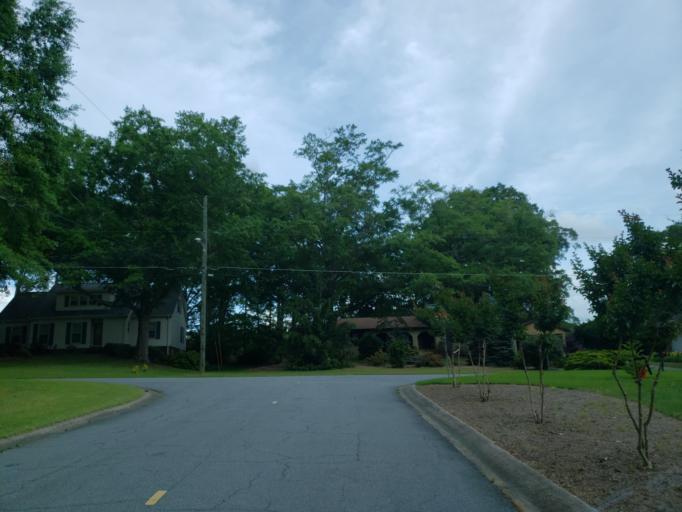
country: US
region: Georgia
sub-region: Cobb County
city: Marietta
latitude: 33.9542
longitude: -84.5667
